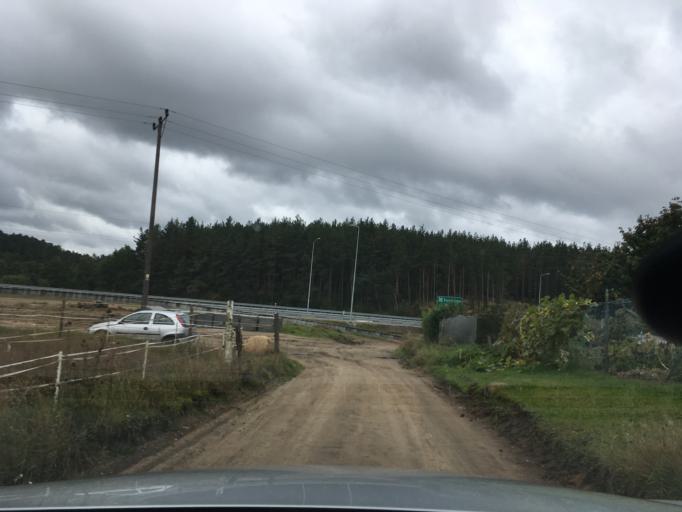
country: PL
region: Pomeranian Voivodeship
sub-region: Powiat koscierski
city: Koscierzyna
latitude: 54.1109
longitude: 17.9914
